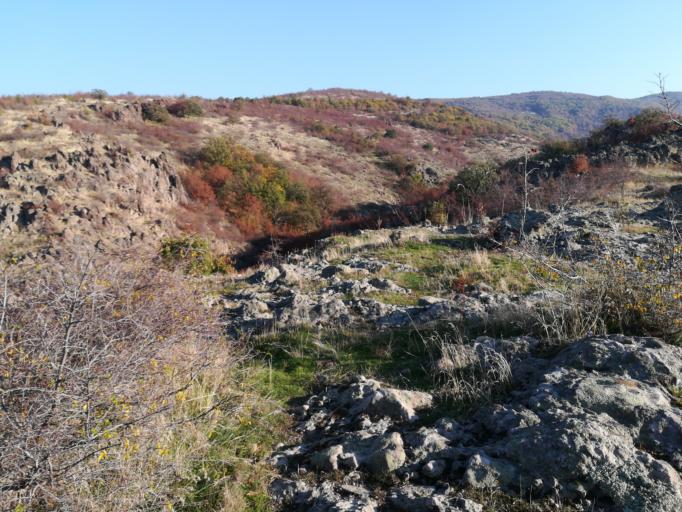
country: BG
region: Khaskovo
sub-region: Obshtina Mineralni Bani
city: Mineralni Bani
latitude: 41.9789
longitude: 25.2385
